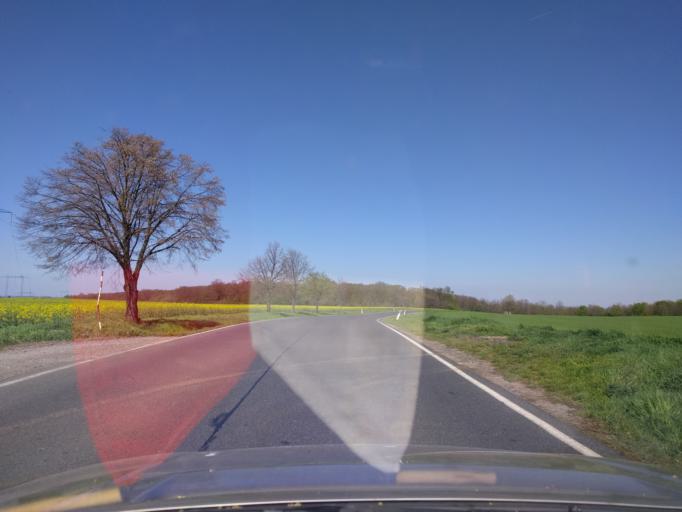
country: CZ
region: Central Bohemia
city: Cesky Brod
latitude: 50.0994
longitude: 14.8619
